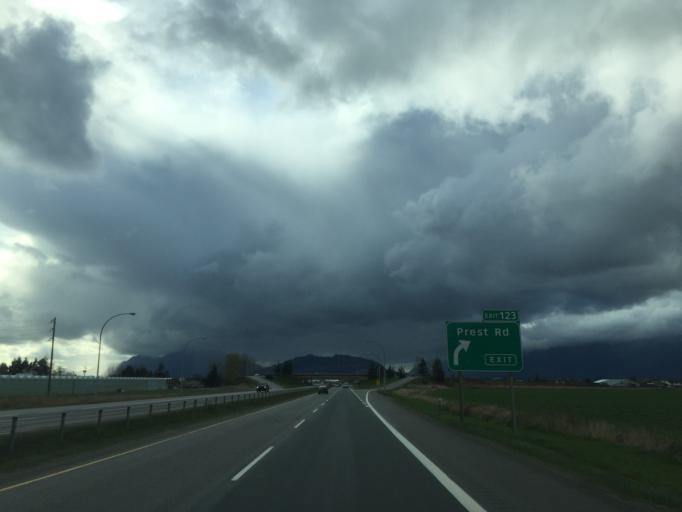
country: CA
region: British Columbia
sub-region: Fraser Valley Regional District
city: Chilliwack
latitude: 49.1553
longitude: -121.9113
